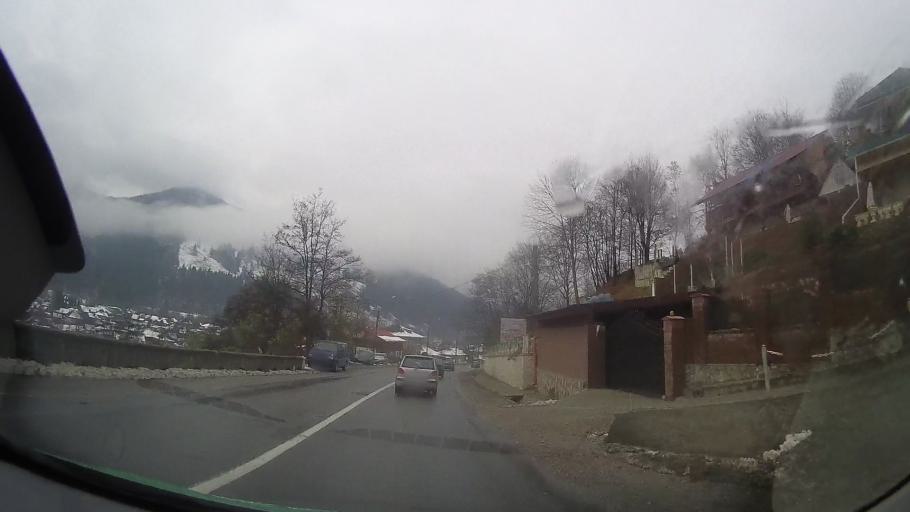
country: RO
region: Neamt
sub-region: Comuna Bicaz
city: Dodeni
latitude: 46.9029
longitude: 26.1134
